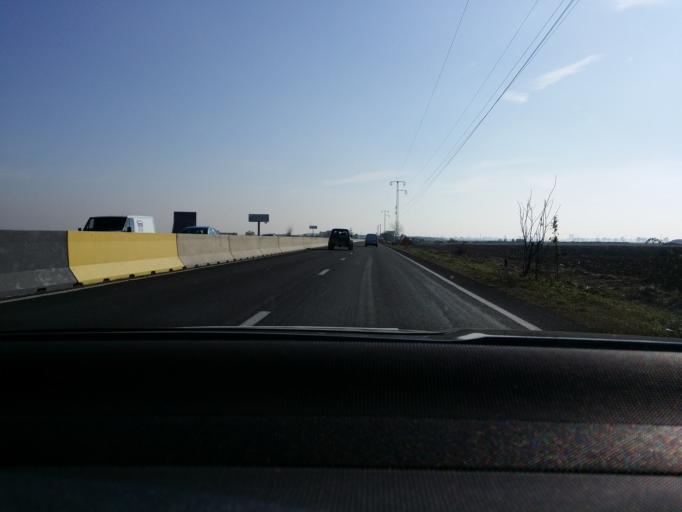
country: RO
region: Prahova
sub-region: Comuna Paulesti
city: Gageni
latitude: 44.9773
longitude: 25.9418
